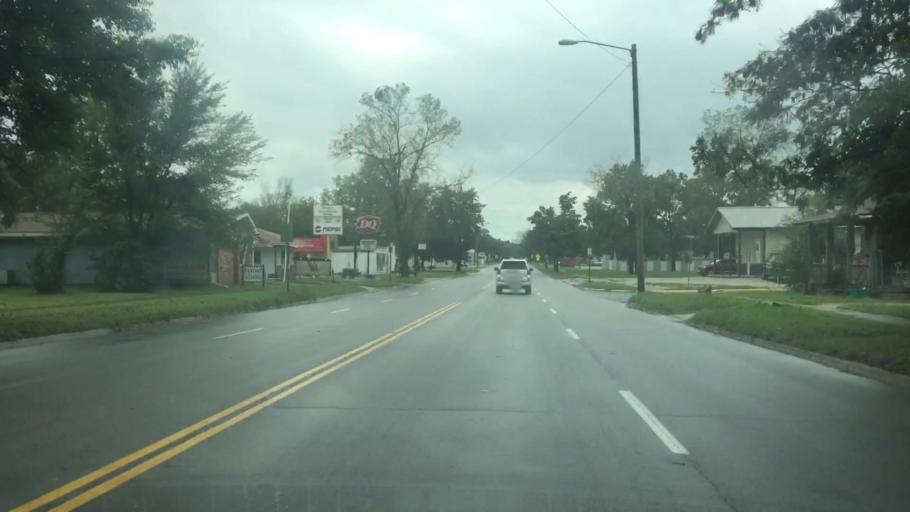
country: US
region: Kansas
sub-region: Allen County
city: Iola
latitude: 37.9197
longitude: -95.4091
